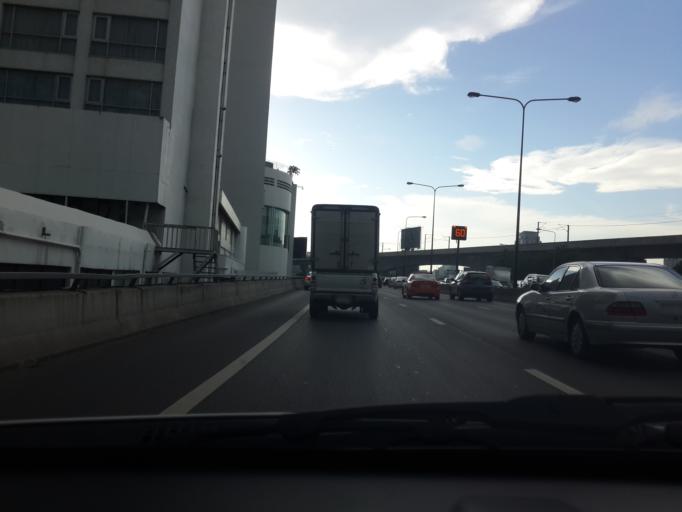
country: TH
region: Bangkok
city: Ratchathewi
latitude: 13.7528
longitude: 100.5478
